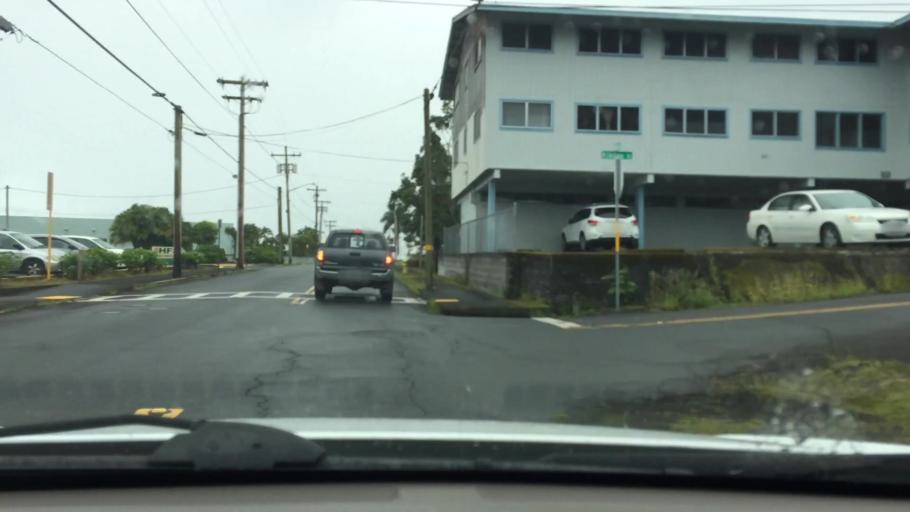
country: US
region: Hawaii
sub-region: Hawaii County
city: Hilo
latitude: 19.7180
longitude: -155.0862
